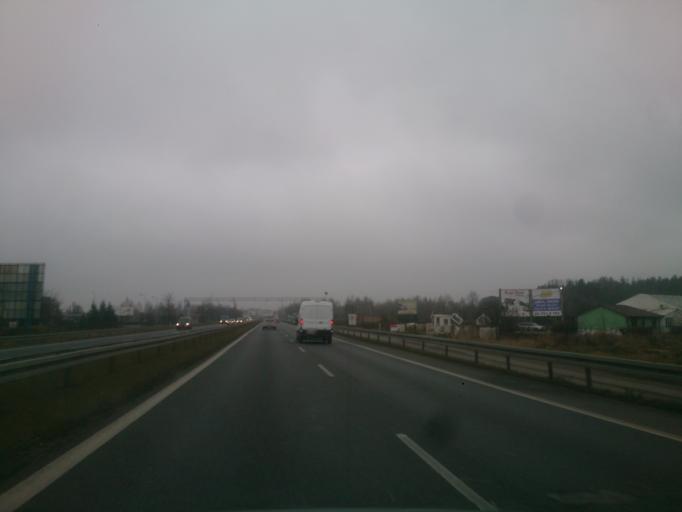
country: PL
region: Masovian Voivodeship
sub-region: Powiat warszawski zachodni
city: Kielpin
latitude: 52.3460
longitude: 20.8622
